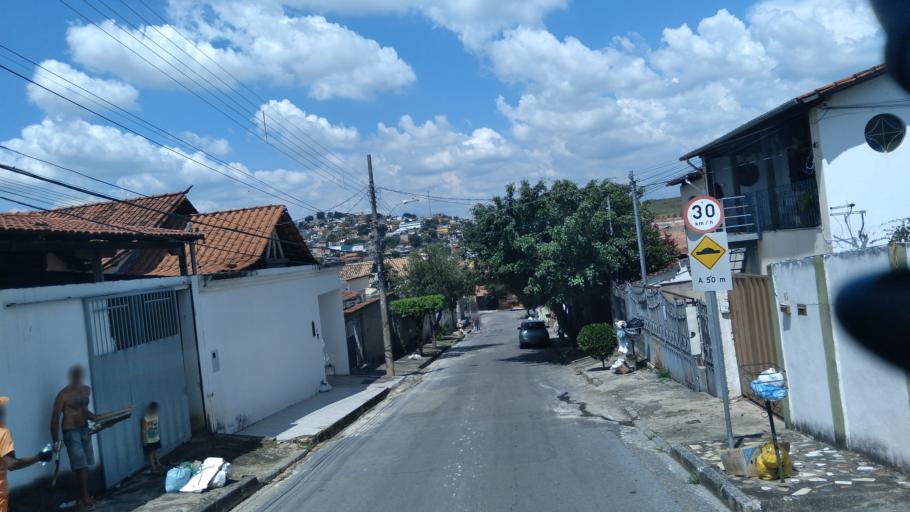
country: BR
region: Minas Gerais
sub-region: Contagem
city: Contagem
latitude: -19.9012
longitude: -44.0216
